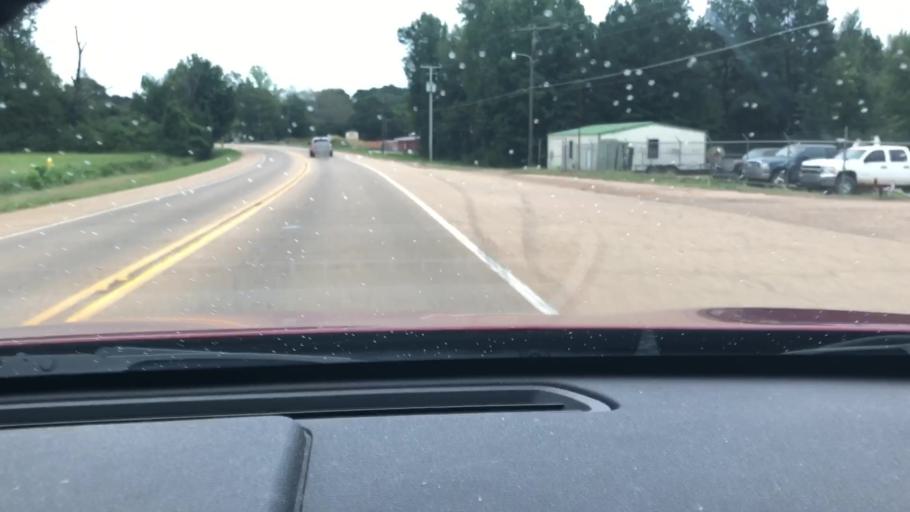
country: US
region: Arkansas
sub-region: Lafayette County
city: Stamps
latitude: 33.3666
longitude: -93.5111
